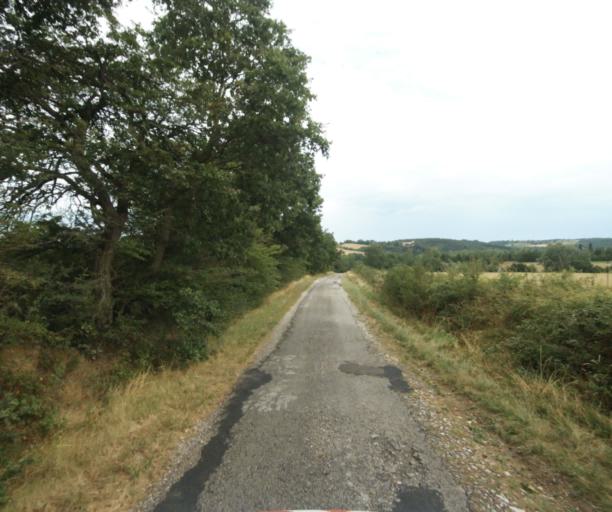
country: FR
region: Midi-Pyrenees
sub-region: Departement de la Haute-Garonne
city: Revel
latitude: 43.4188
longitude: 1.9780
